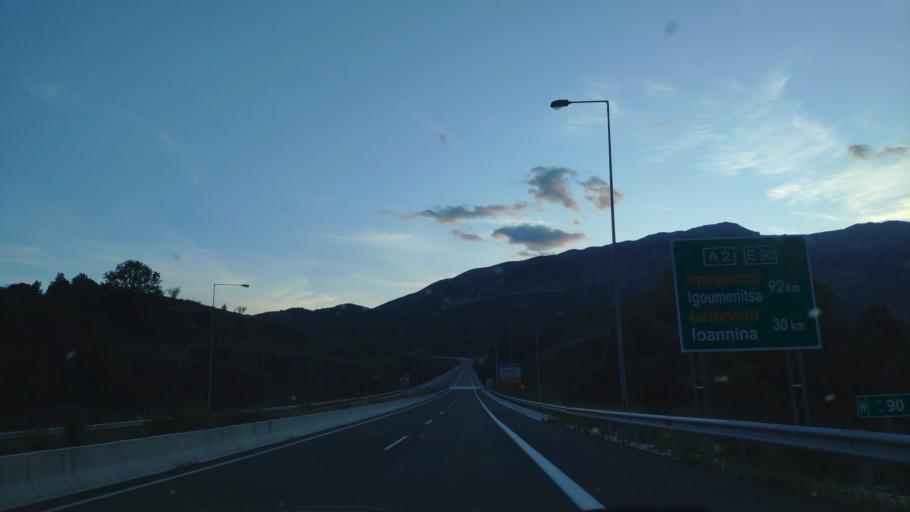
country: GR
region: Epirus
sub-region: Nomos Ioanninon
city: Katsikas
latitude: 39.7162
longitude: 20.9903
